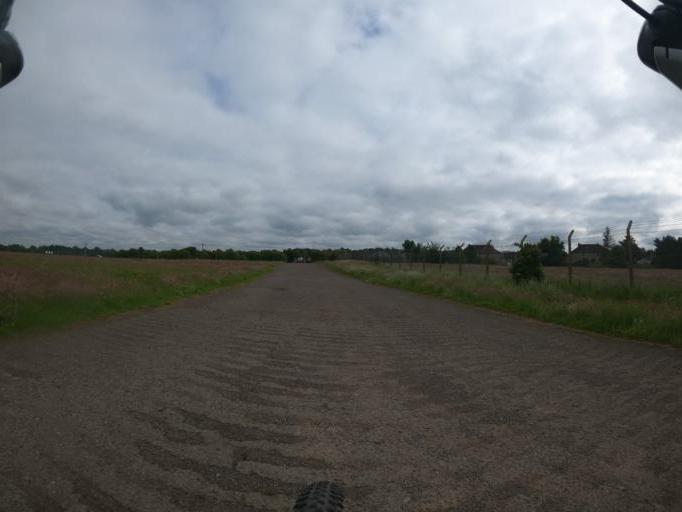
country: GB
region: Scotland
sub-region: Edinburgh
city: Newbridge
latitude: 55.9402
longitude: -3.3895
